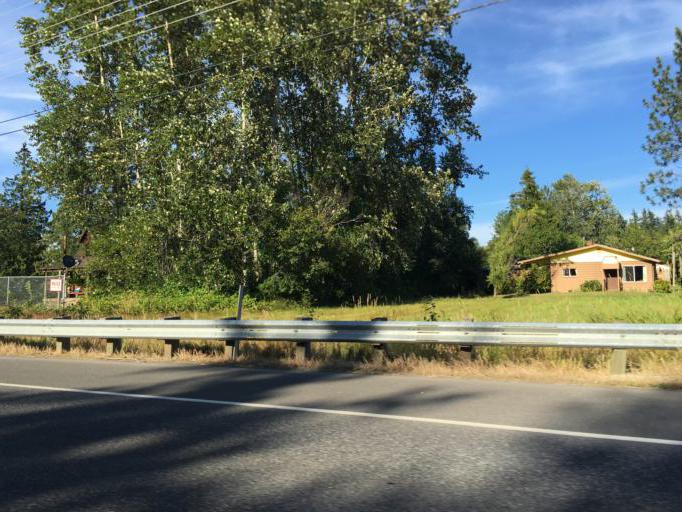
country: US
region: Washington
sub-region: Whatcom County
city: Bellingham
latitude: 48.8217
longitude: -122.4859
